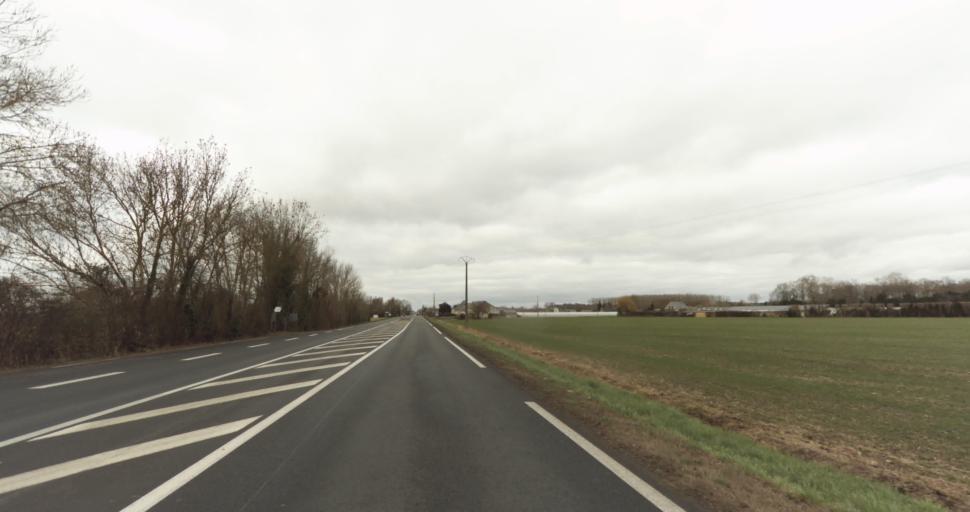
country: FR
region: Pays de la Loire
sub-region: Departement de Maine-et-Loire
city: Vivy
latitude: 47.3139
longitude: -0.0445
